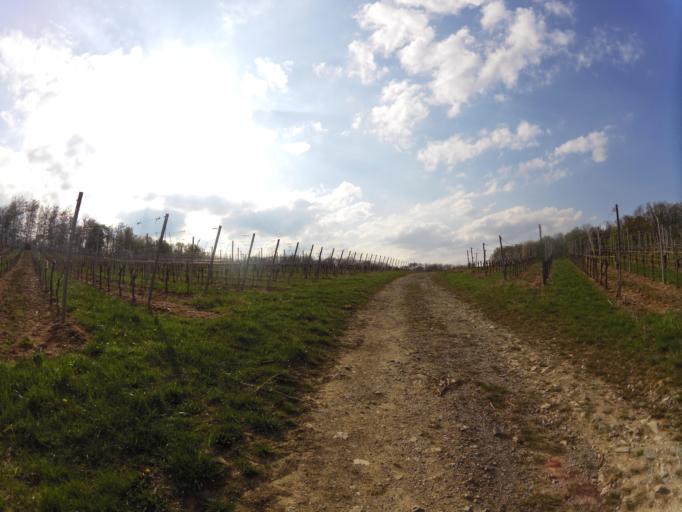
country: DE
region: Bavaria
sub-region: Regierungsbezirk Unterfranken
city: Winterhausen
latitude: 49.6947
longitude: 10.0090
